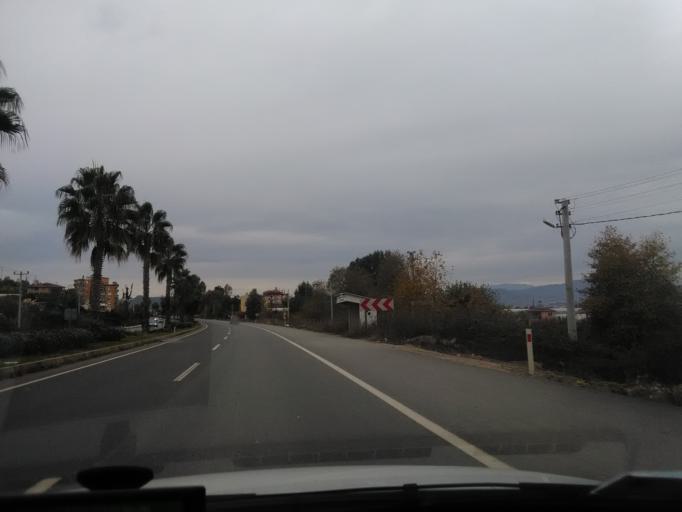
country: TR
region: Antalya
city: Gazipasa
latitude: 36.2534
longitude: 32.3360
